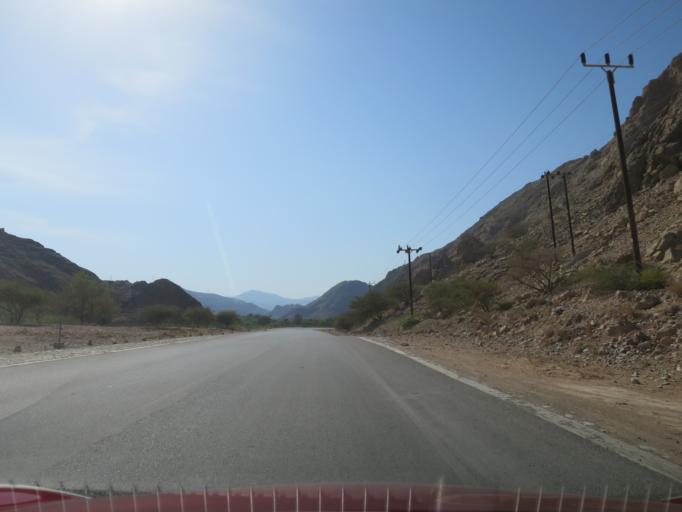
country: OM
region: Muhafazat Masqat
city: Muscat
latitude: 23.5094
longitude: 58.6691
